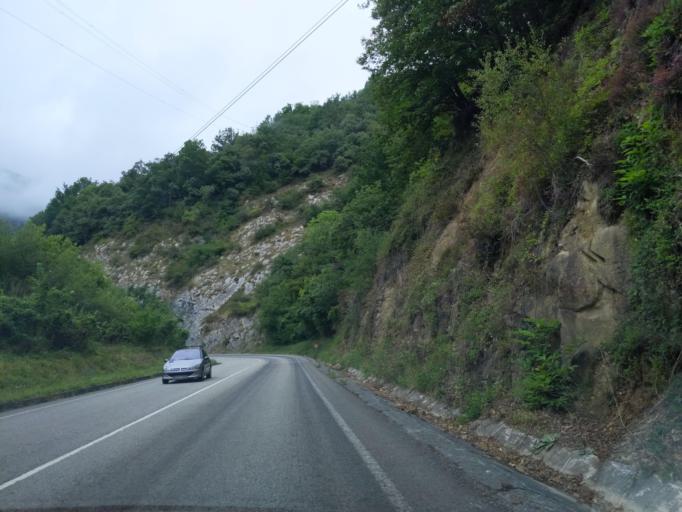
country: ES
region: Asturias
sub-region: Province of Asturias
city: Pola de Laviana
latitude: 43.2274
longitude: -5.4638
